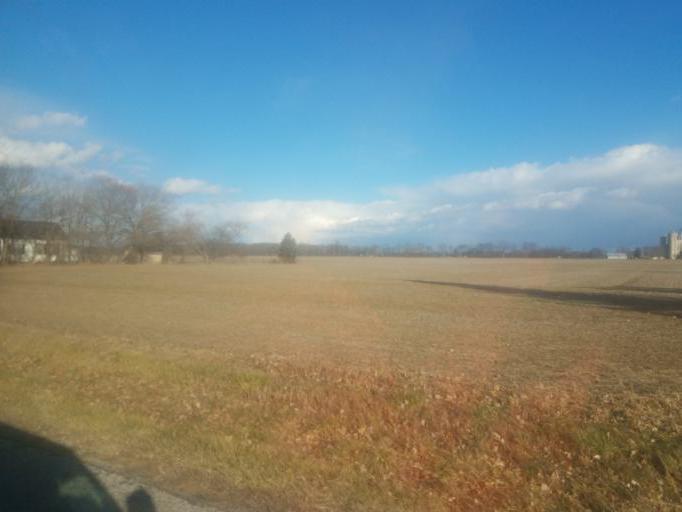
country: US
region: Ohio
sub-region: Marion County
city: Prospect
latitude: 40.3857
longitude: -83.1457
